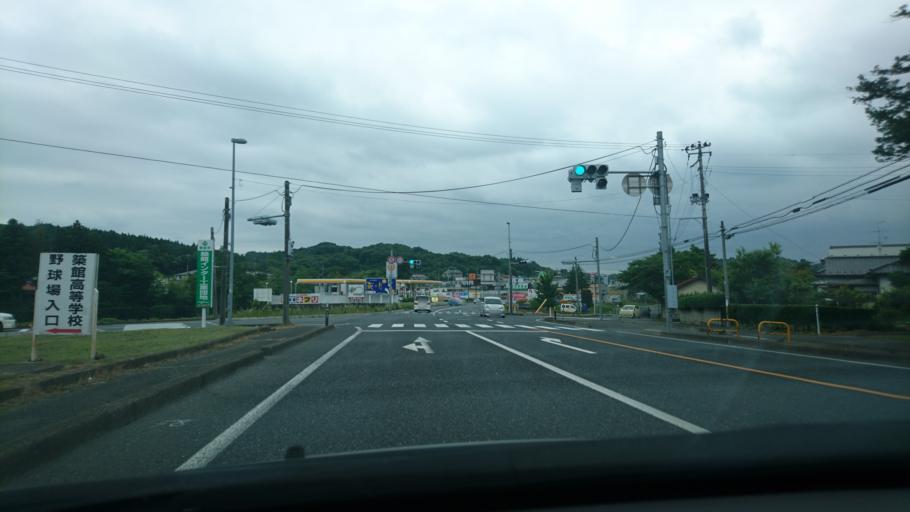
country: JP
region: Miyagi
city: Furukawa
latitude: 38.7139
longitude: 141.0210
